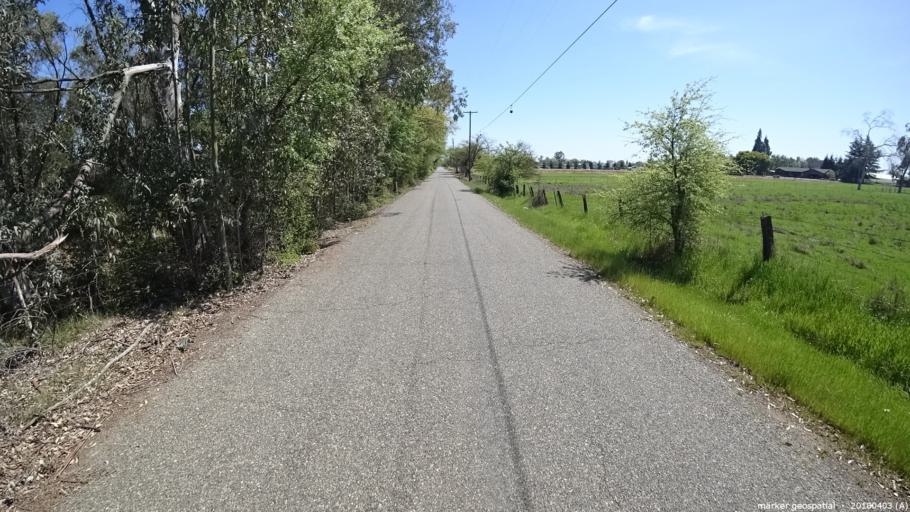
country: US
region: California
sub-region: Sacramento County
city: Wilton
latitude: 38.4026
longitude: -121.2856
